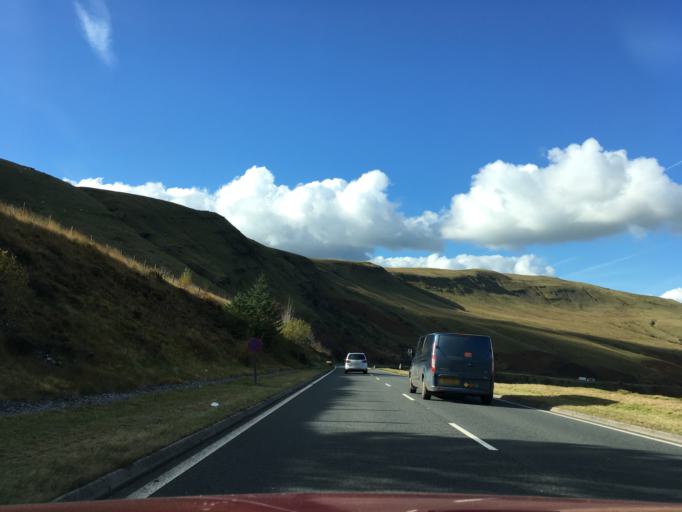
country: GB
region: Wales
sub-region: Sir Powys
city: Brecon
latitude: 51.8736
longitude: -3.4892
